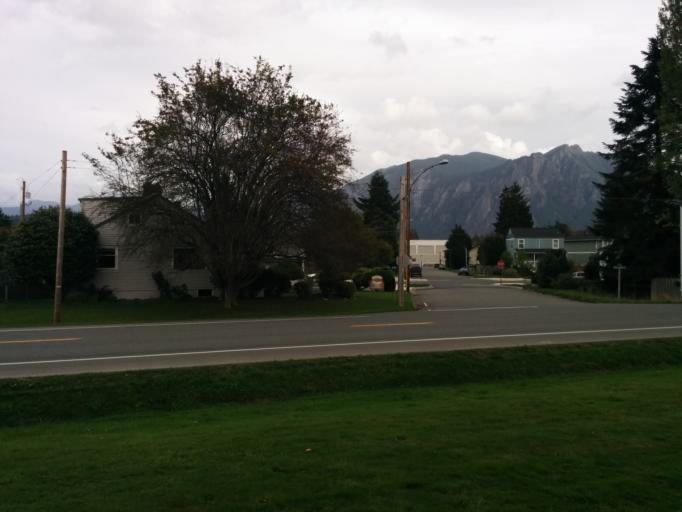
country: US
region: Washington
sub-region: King County
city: Snoqualmie
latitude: 47.5225
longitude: -121.8209
